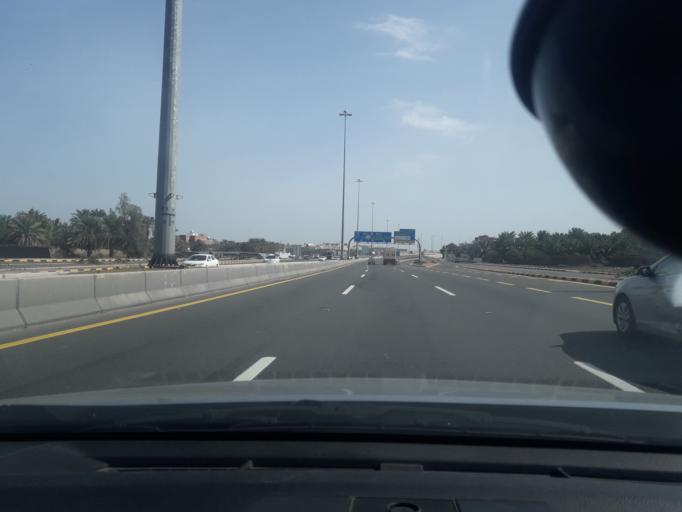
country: SA
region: Al Madinah al Munawwarah
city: Medina
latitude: 24.4421
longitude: 39.6327
